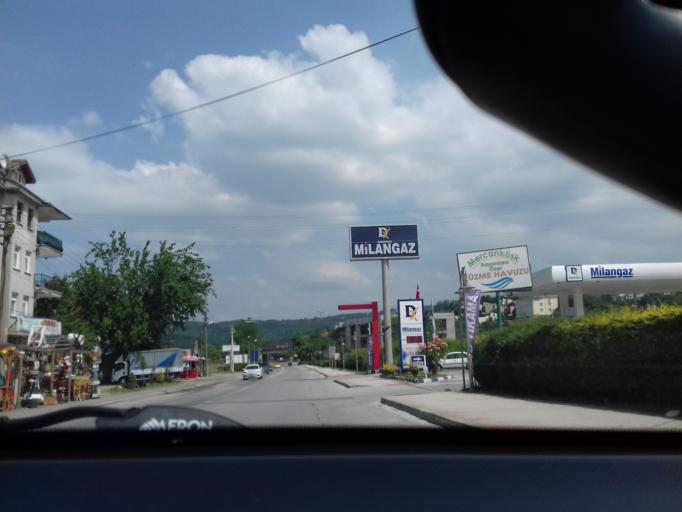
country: TR
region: Sakarya
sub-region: Merkez
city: Sapanca
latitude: 40.6897
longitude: 30.2757
